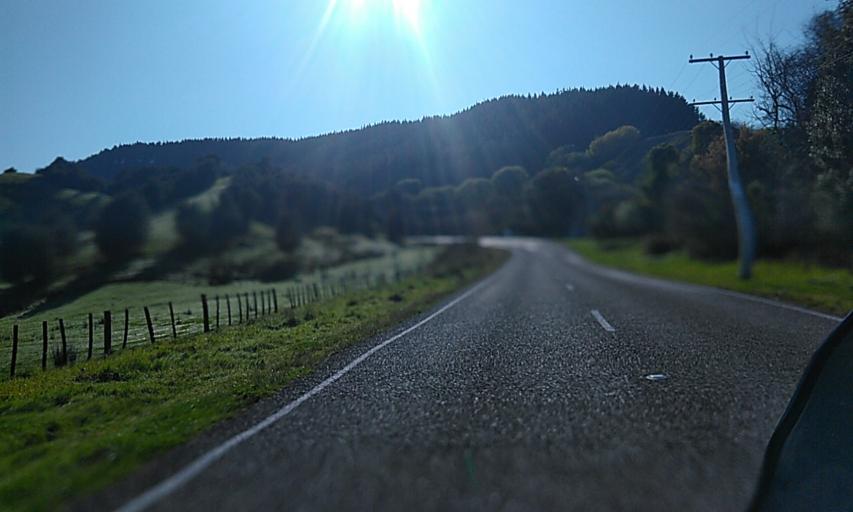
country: NZ
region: Gisborne
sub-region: Gisborne District
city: Gisborne
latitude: -38.5948
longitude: 177.9696
